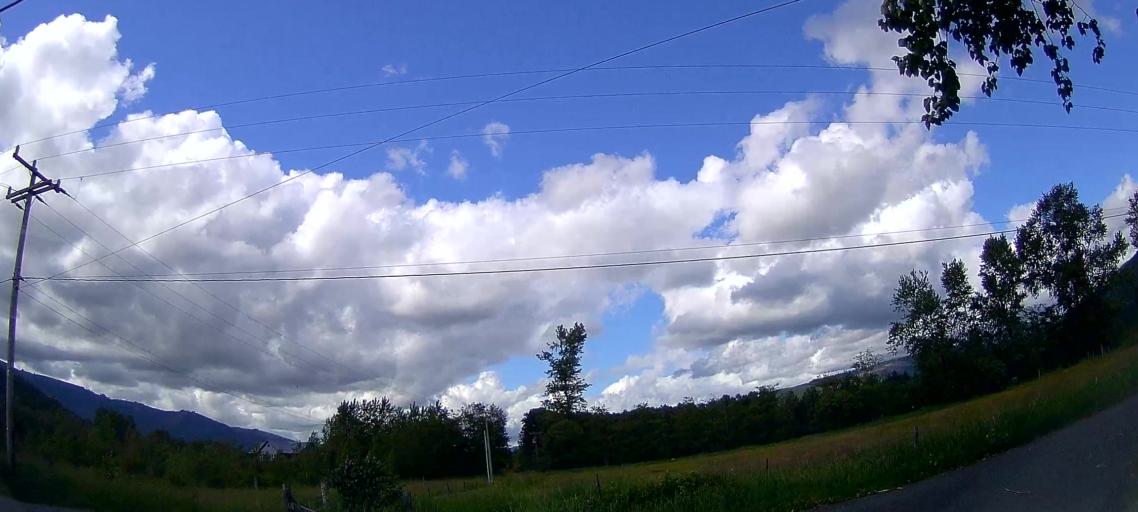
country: US
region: Washington
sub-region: Whatcom County
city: Sudden Valley
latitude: 48.6929
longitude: -122.1881
